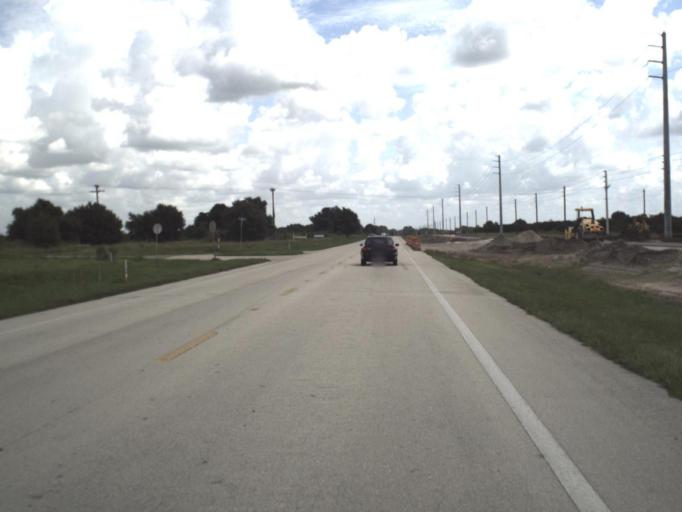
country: US
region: Florida
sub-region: DeSoto County
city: Nocatee
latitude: 27.1216
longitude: -81.9146
